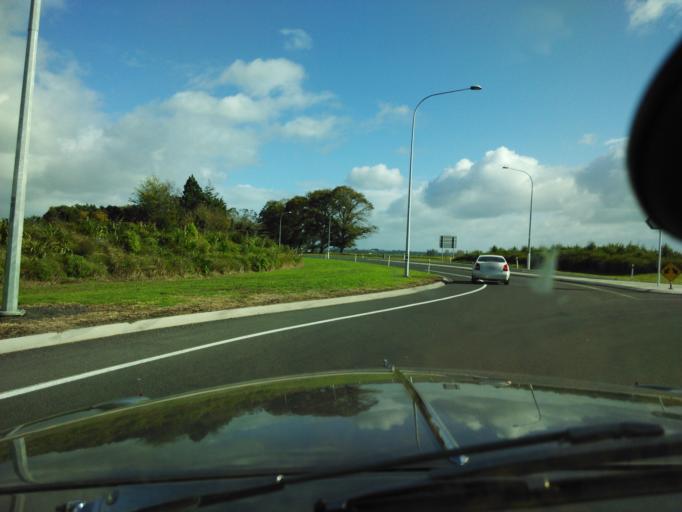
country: NZ
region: Waikato
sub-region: Matamata-Piako District
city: Matamata
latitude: -37.6218
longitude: 175.5957
